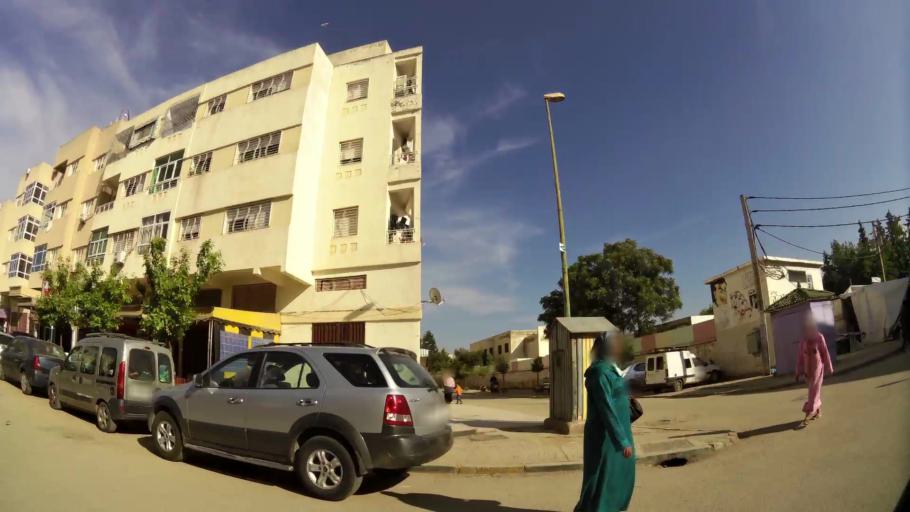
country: MA
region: Fes-Boulemane
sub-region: Fes
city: Fes
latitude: 34.0219
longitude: -5.0326
